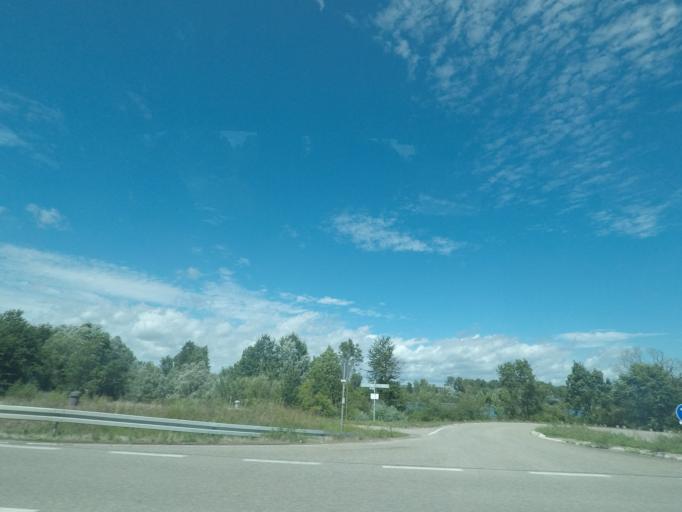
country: FR
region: Alsace
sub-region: Departement du Bas-Rhin
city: Plobsheim
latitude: 48.4943
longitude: 7.7946
